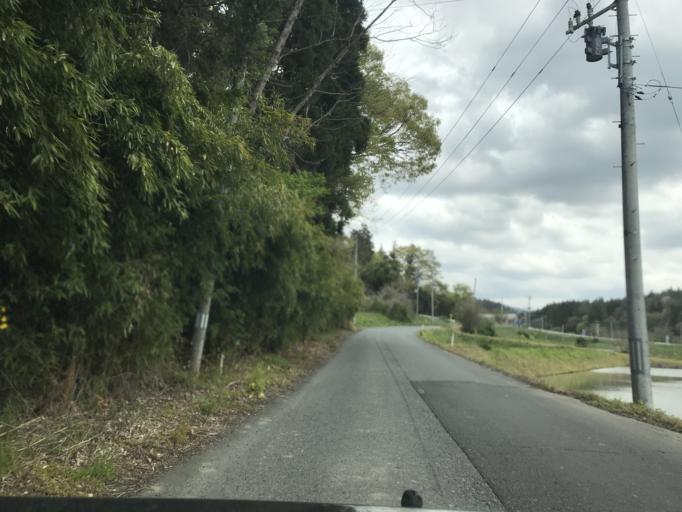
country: JP
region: Iwate
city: Ichinoseki
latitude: 38.8432
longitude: 141.3486
